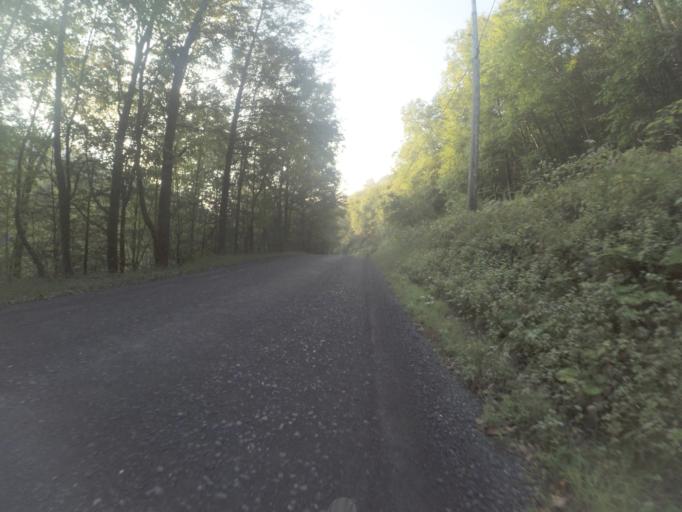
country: US
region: Pennsylvania
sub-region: Mifflin County
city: Milroy
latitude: 40.8504
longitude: -77.4568
